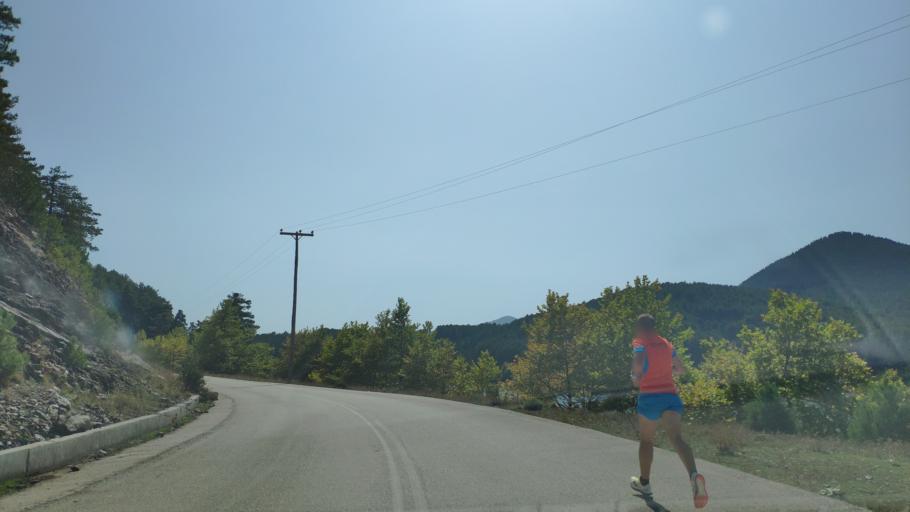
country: GR
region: West Greece
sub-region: Nomos Achaias
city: Kalavryta
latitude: 37.9298
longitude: 22.2902
